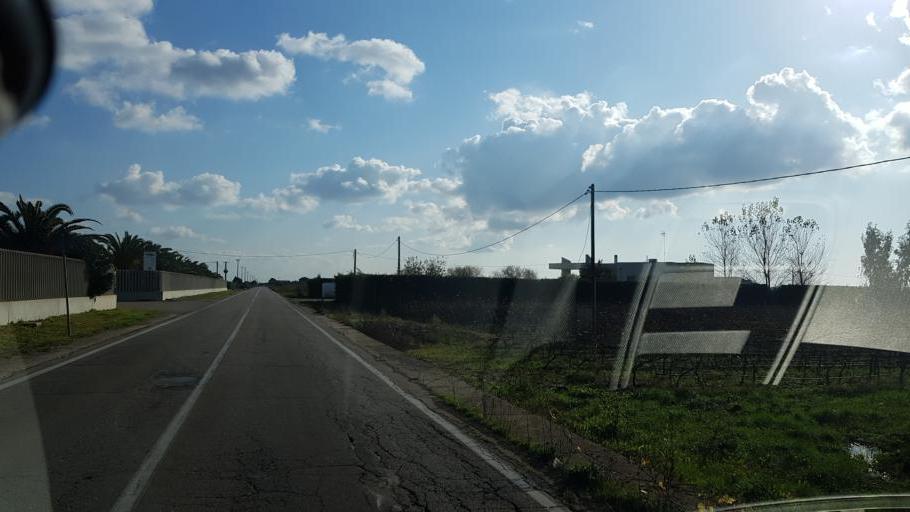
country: IT
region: Apulia
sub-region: Provincia di Lecce
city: Veglie
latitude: 40.3210
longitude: 17.9787
